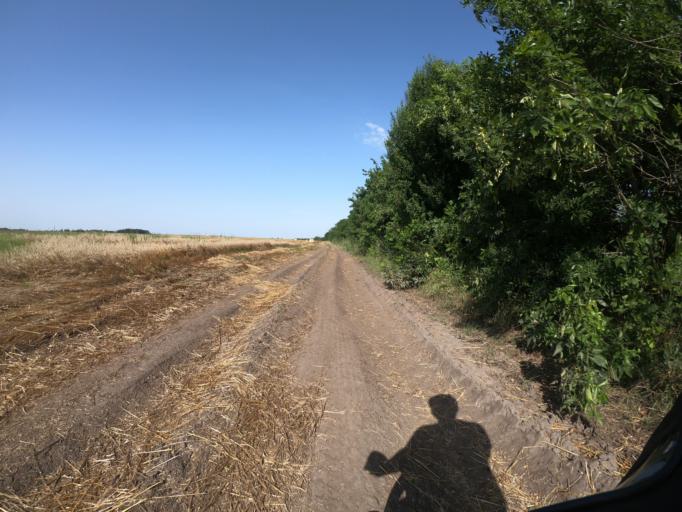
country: HU
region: Hajdu-Bihar
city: Egyek
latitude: 47.5820
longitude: 20.9532
